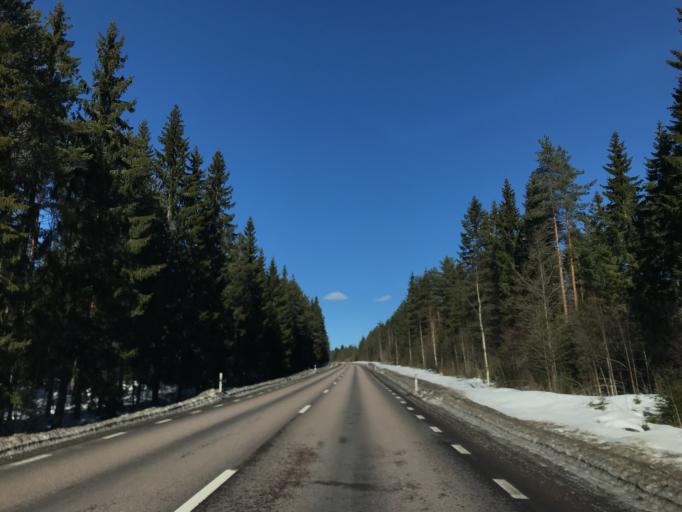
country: SE
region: Vaermland
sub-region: Filipstads Kommun
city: Filipstad
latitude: 59.7846
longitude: 14.2590
